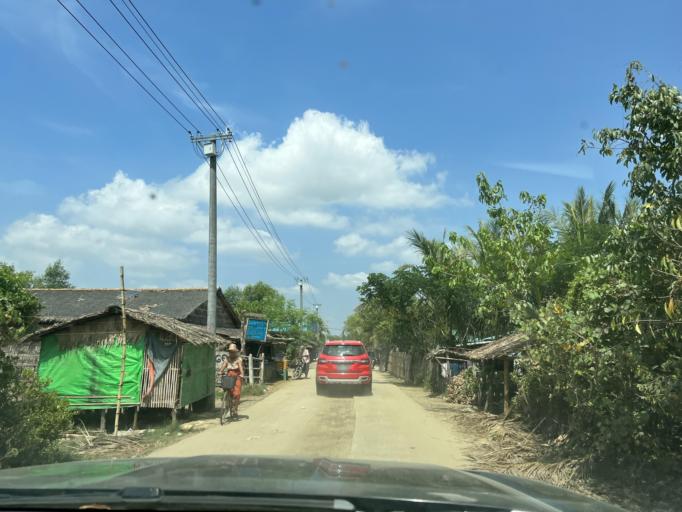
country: MM
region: Ayeyarwady
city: Pyapon
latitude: 15.9043
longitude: 95.6145
